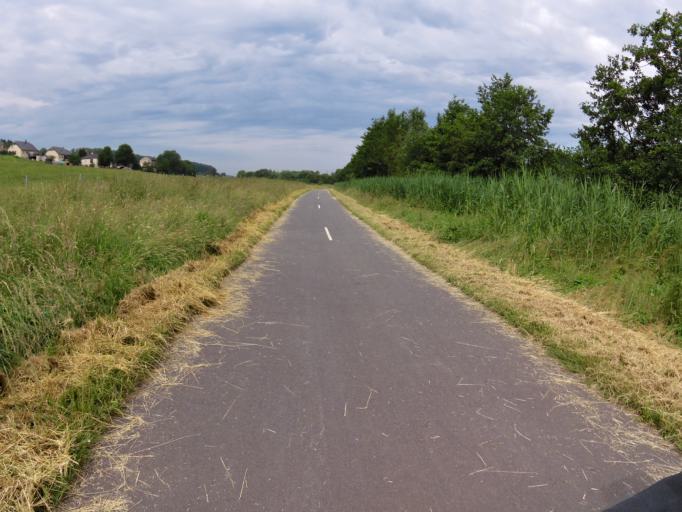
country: FR
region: Champagne-Ardenne
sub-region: Departement des Ardennes
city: Donchery
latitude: 49.6926
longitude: 4.8855
